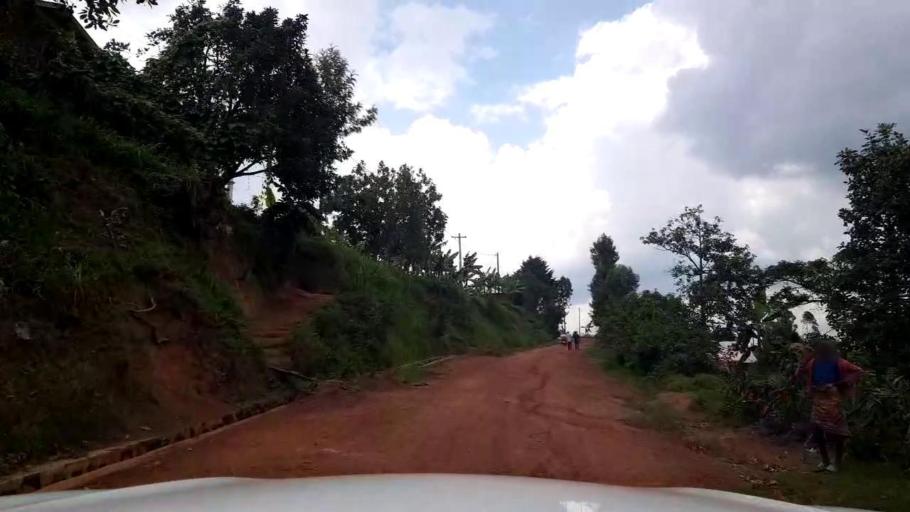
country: RW
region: Northern Province
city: Byumba
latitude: -1.4873
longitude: 29.9092
